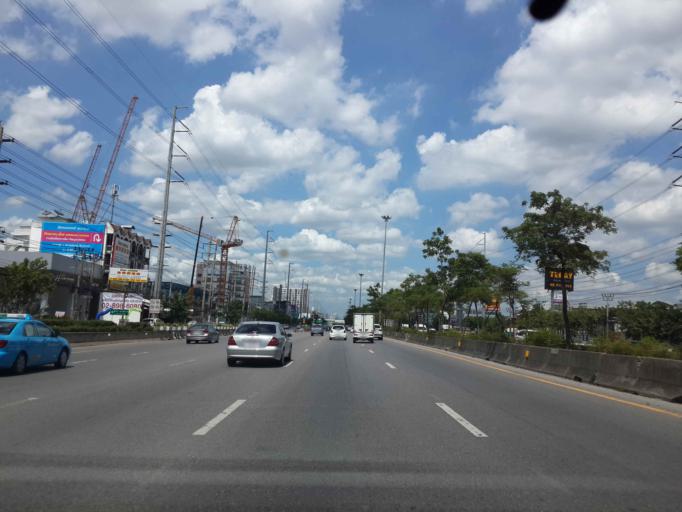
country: TH
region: Bangkok
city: Bang Khun Thian
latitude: 13.6692
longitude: 100.4505
